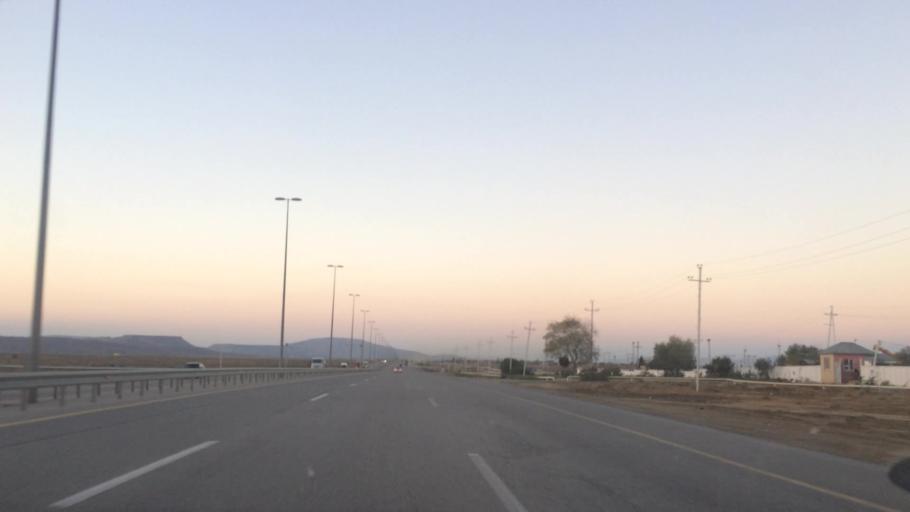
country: AZ
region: Baki
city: Qobustan
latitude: 40.0005
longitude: 49.4292
